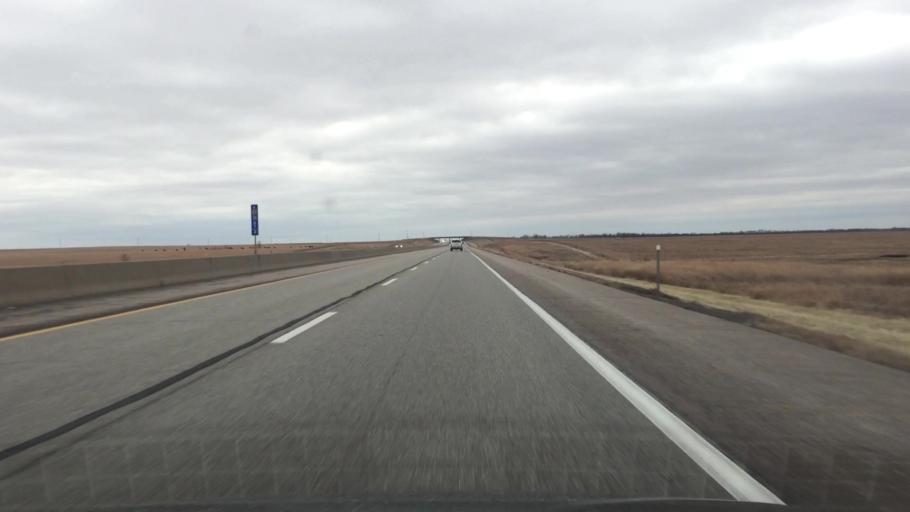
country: US
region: Kansas
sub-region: Butler County
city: El Dorado
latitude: 37.9935
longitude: -96.6980
